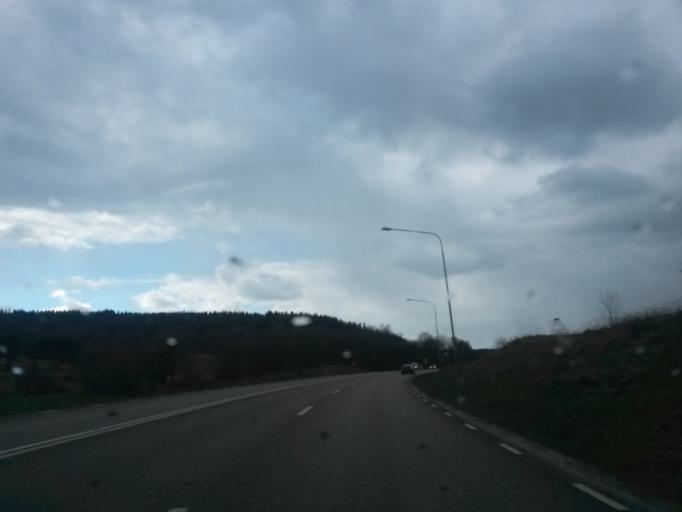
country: SE
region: Vaestra Goetaland
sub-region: Skovde Kommun
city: Skoevde
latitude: 58.3812
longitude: 13.8136
